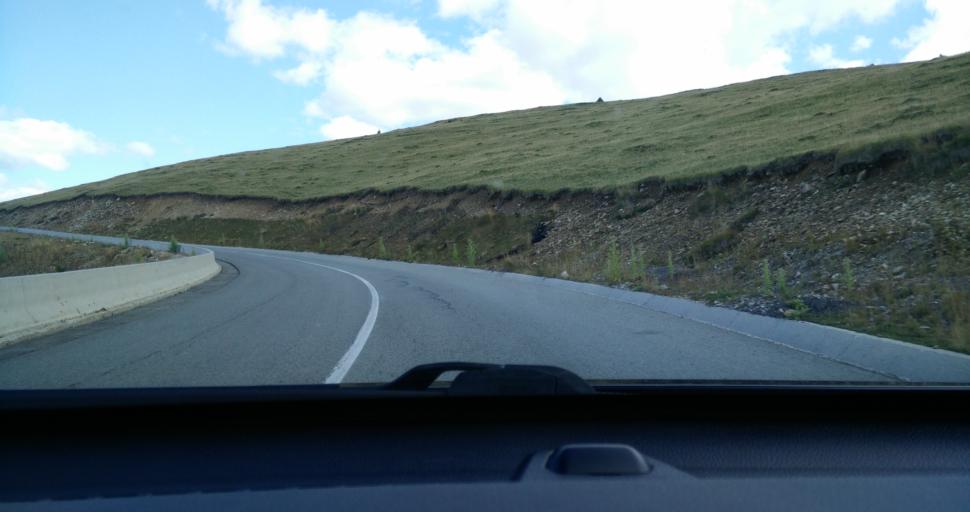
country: RO
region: Gorj
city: Novaci-Straini
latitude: 45.2561
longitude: 23.6976
